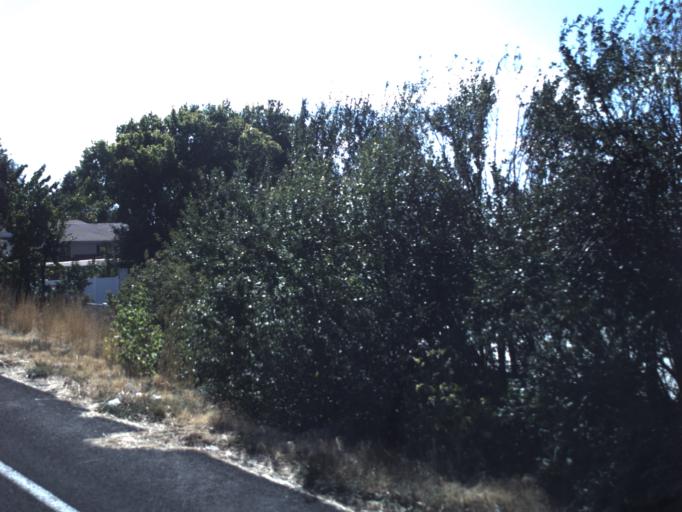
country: US
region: Utah
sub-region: Davis County
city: Woods Cross
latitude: 40.8735
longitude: -111.8892
